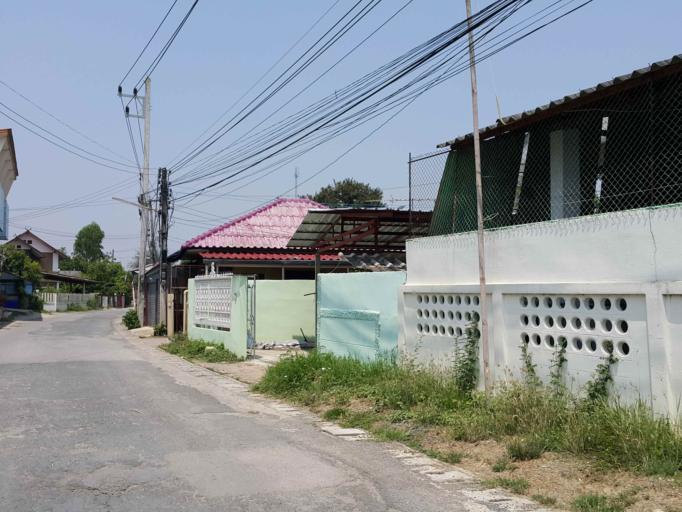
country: TH
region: Chiang Mai
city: San Kamphaeng
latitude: 18.7921
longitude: 99.0849
